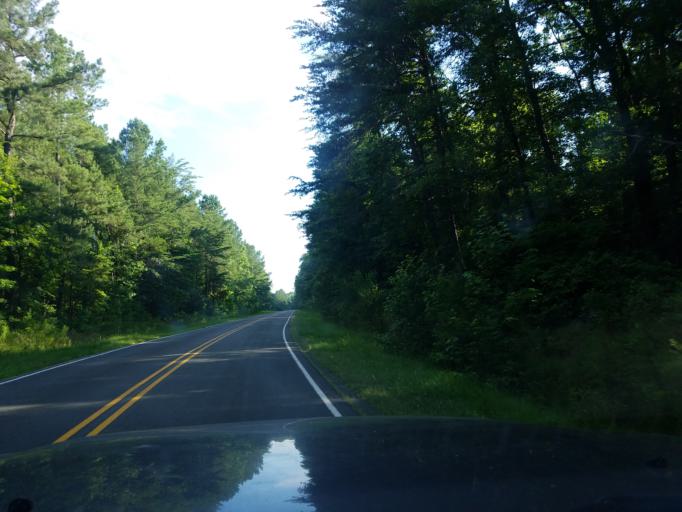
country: US
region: North Carolina
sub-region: Granville County
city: Butner
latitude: 36.1882
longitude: -78.8238
